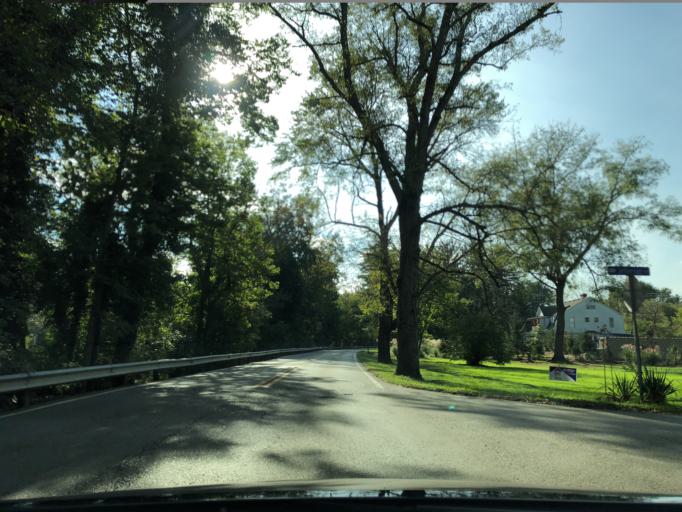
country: US
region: Ohio
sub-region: Hamilton County
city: The Village of Indian Hill
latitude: 39.2521
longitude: -84.2840
